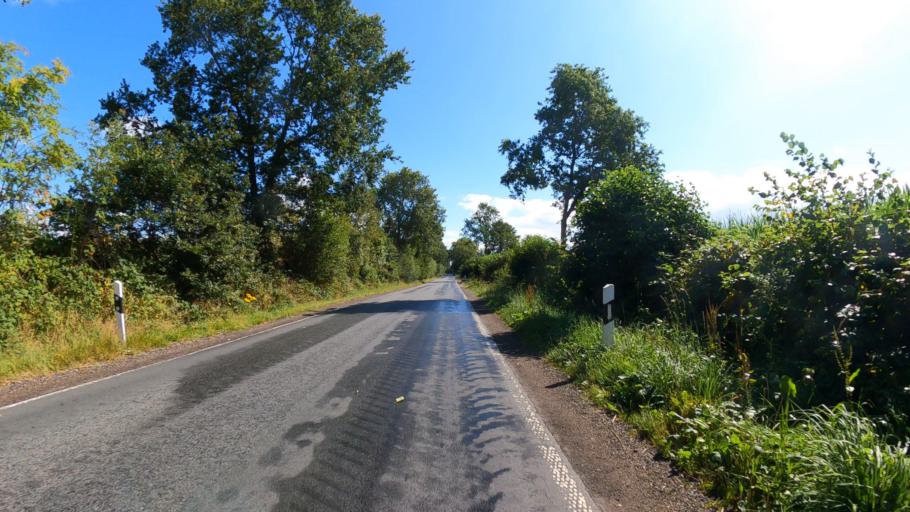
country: DE
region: Schleswig-Holstein
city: Fuhlendorf
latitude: 53.9571
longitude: 9.8836
